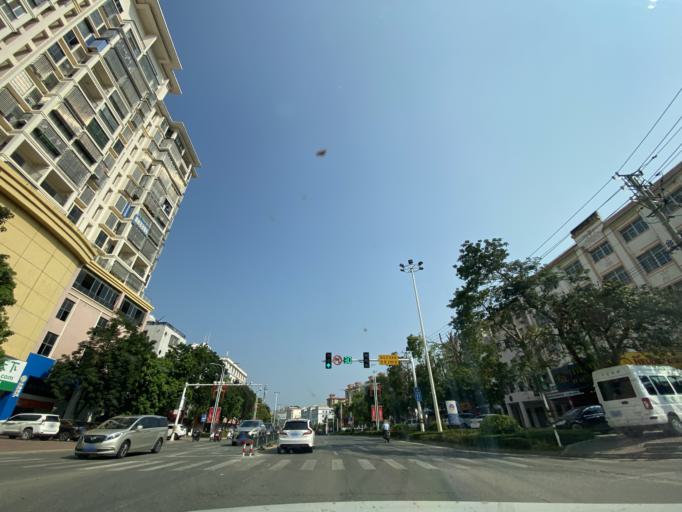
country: CN
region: Hainan
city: Chongshan
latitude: 18.7678
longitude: 109.5182
